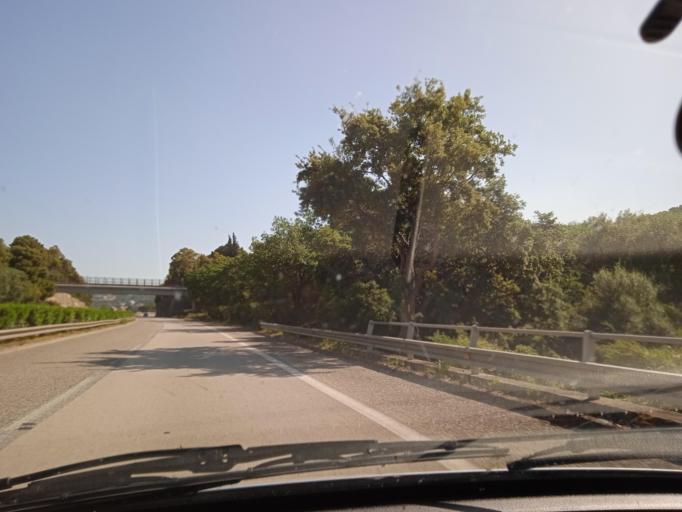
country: IT
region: Sicily
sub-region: Messina
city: Capo d'Orlando
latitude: 38.1247
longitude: 14.7299
